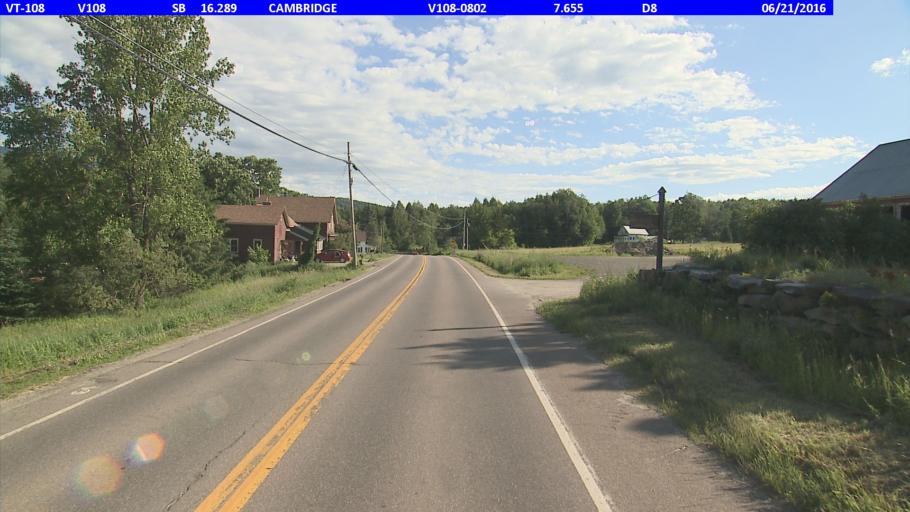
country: US
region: Vermont
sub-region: Lamoille County
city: Johnson
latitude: 44.6295
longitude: -72.8306
